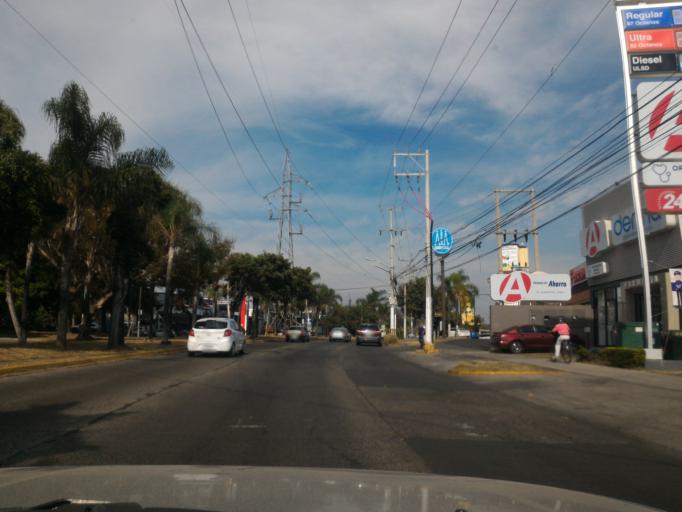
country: MX
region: Jalisco
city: Zapopan2
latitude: 20.6883
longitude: -103.4197
